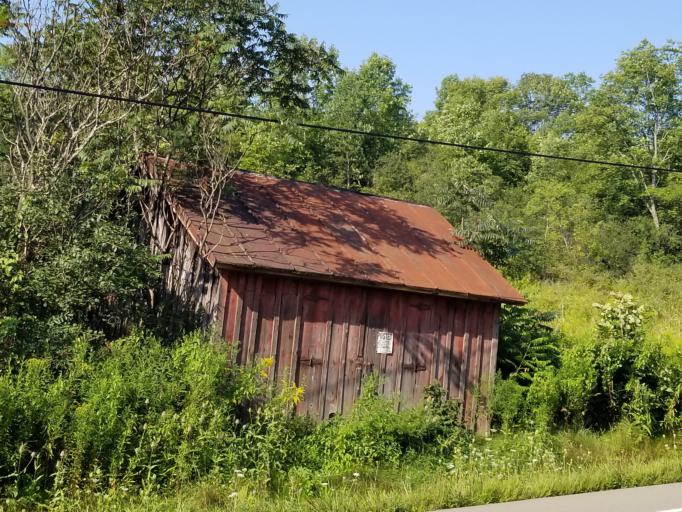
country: US
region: New York
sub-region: Allegany County
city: Belmont
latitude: 42.2962
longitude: -78.0770
